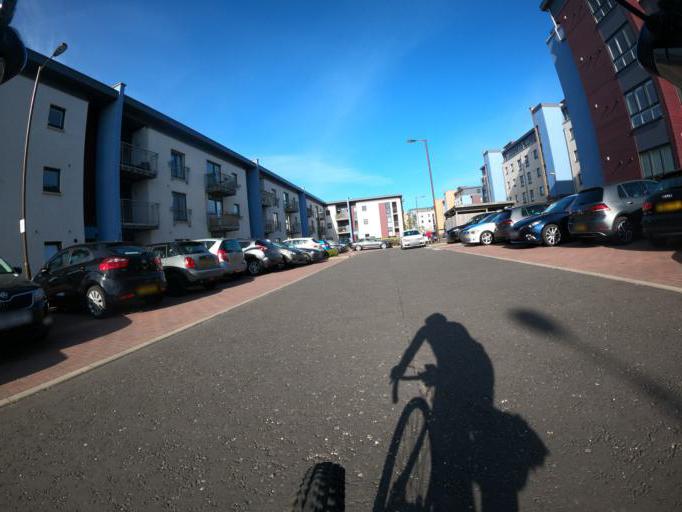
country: GB
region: Scotland
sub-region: Edinburgh
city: Edinburgh
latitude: 55.9722
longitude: -3.2293
